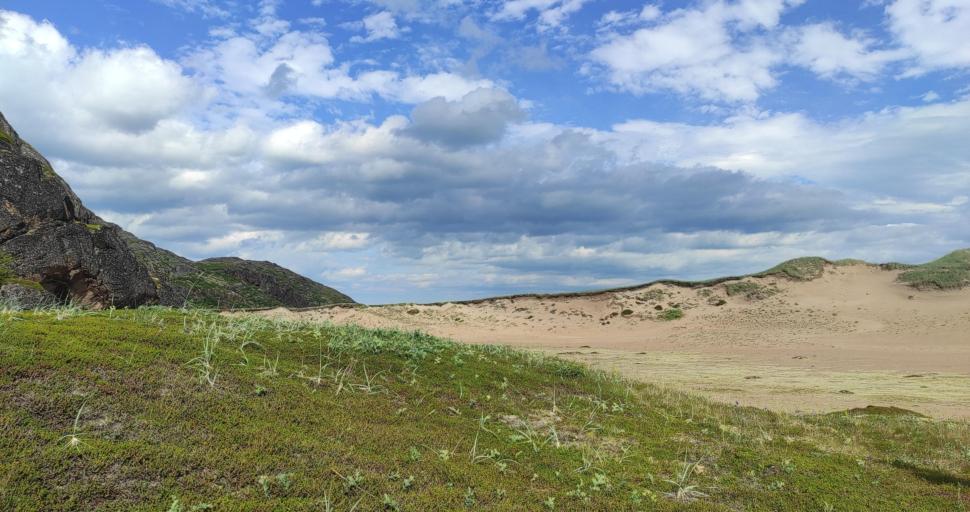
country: RU
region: Murmansk
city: Teriberka
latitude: 69.1719
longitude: 35.7658
